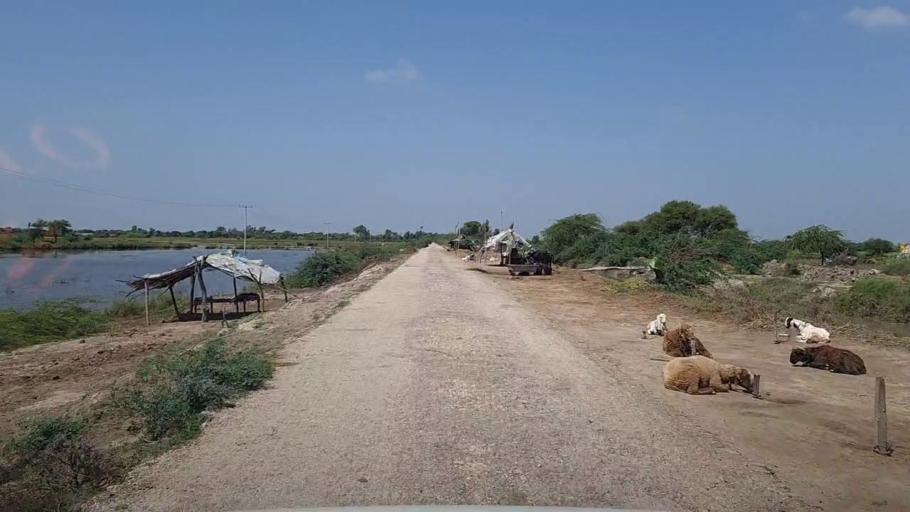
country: PK
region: Sindh
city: Kario
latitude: 24.8861
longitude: 68.6817
